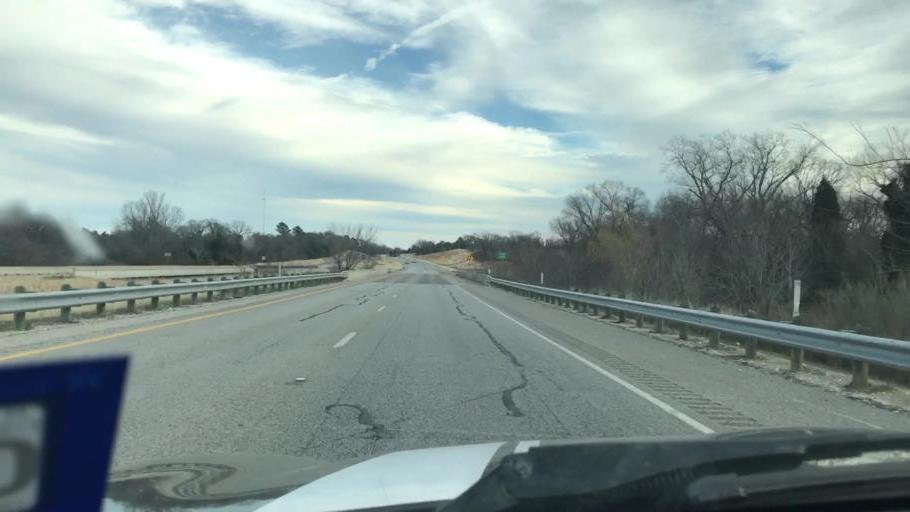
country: US
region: Texas
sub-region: Bastrop County
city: Elgin
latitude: 30.3050
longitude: -97.2979
